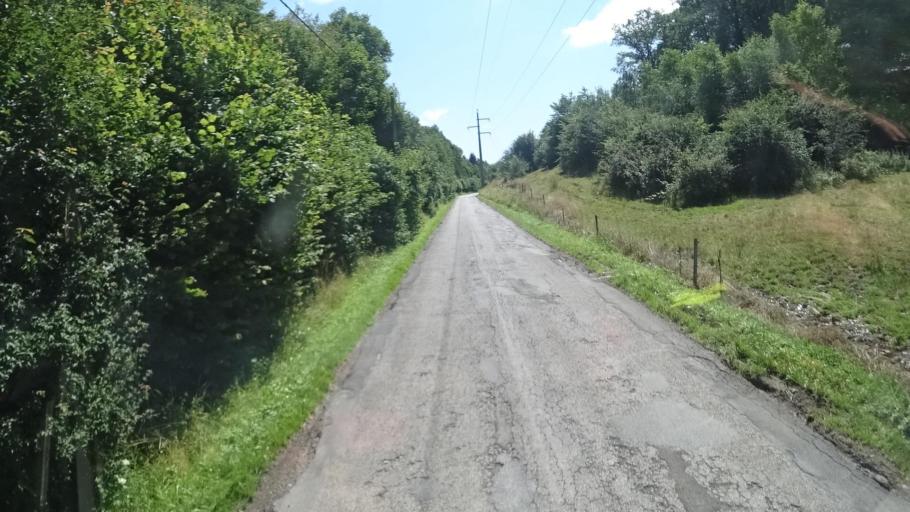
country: BE
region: Wallonia
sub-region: Province de Namur
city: Profondeville
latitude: 50.3631
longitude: 4.8214
